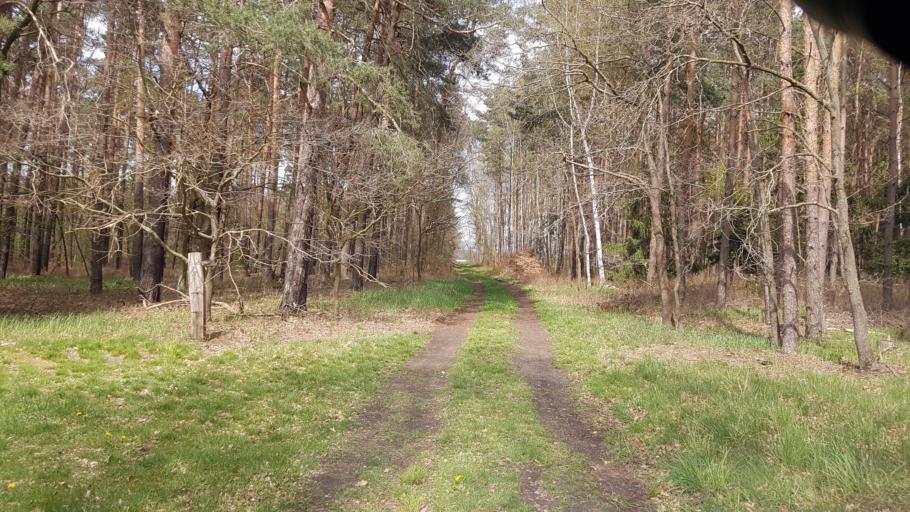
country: DE
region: Brandenburg
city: Bronkow
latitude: 51.6098
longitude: 13.9306
